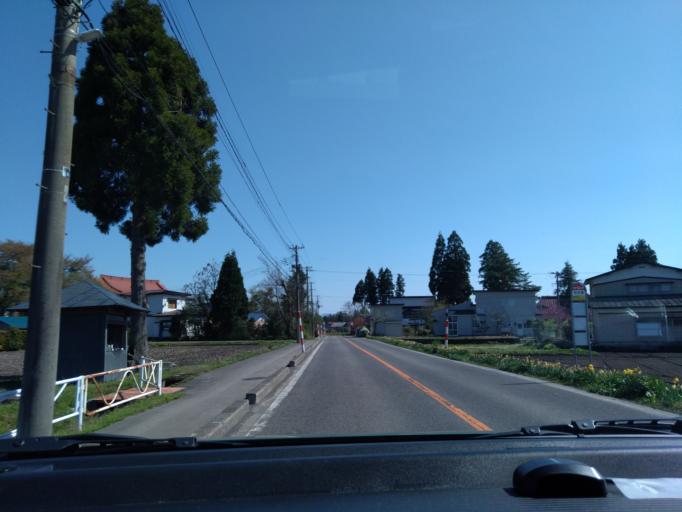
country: JP
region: Akita
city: Kakunodatemachi
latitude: 39.5621
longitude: 140.5841
